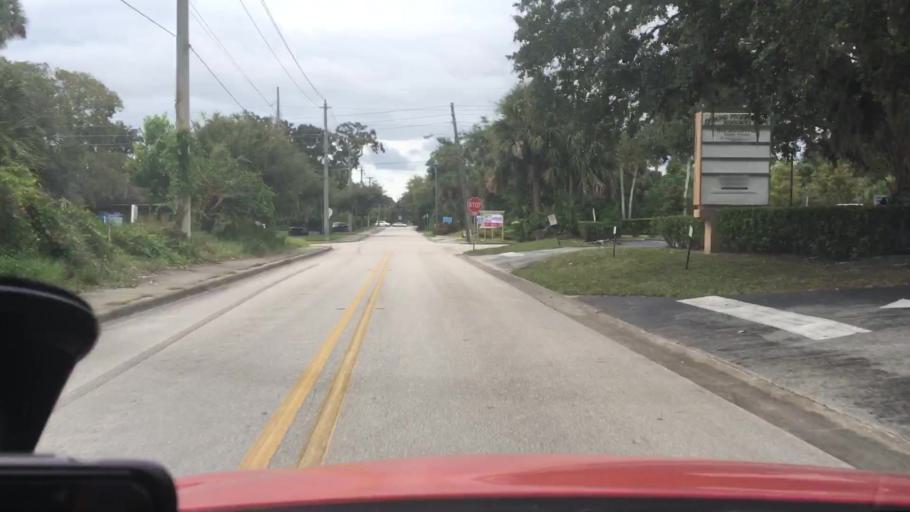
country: US
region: Florida
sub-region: Volusia County
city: Ormond Beach
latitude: 29.2813
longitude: -81.0817
